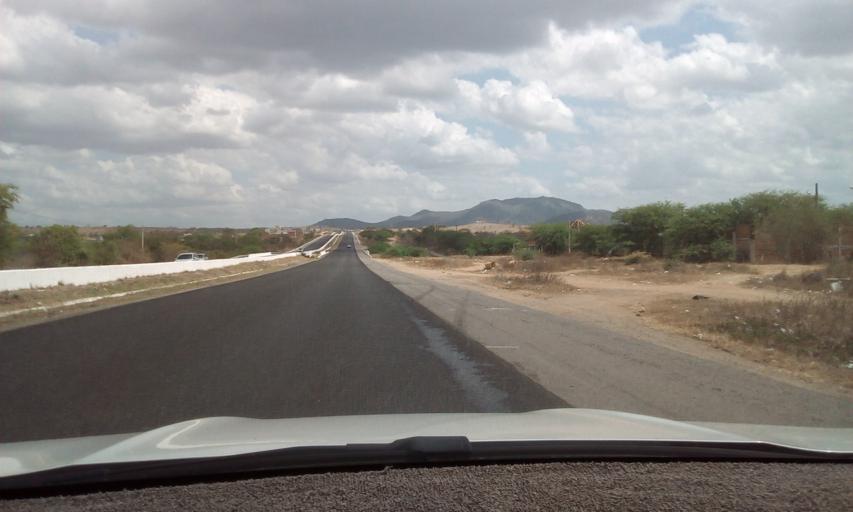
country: BR
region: Pernambuco
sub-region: Toritama
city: Toritama
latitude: -8.0334
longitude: -36.0528
